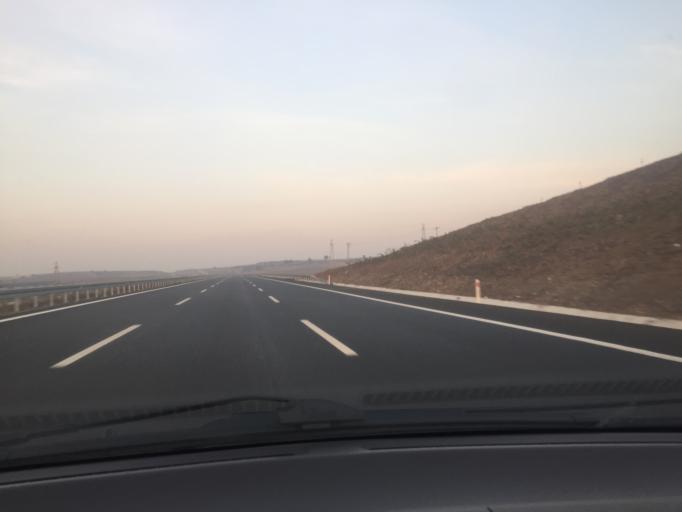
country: TR
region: Bursa
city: Mahmudiye
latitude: 40.2674
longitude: 28.6392
